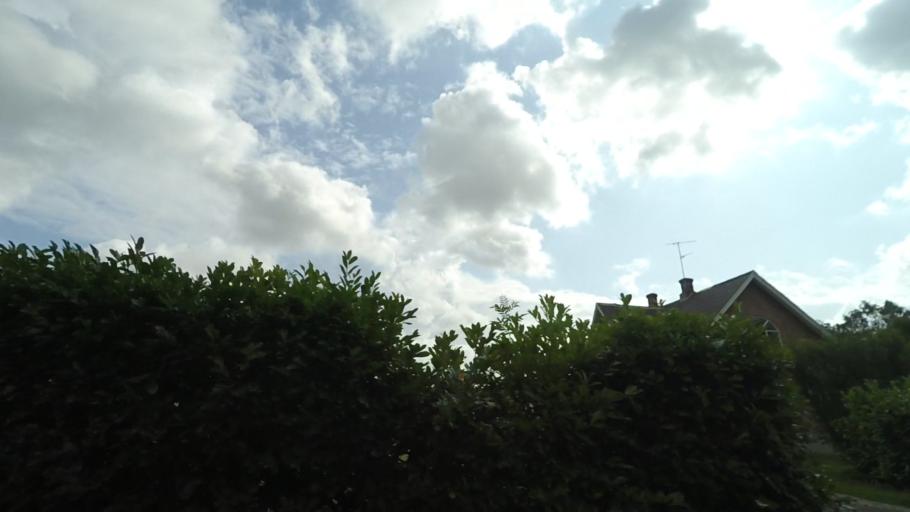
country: DK
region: Central Jutland
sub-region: Syddjurs Kommune
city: Ryomgard
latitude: 56.4821
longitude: 10.4847
